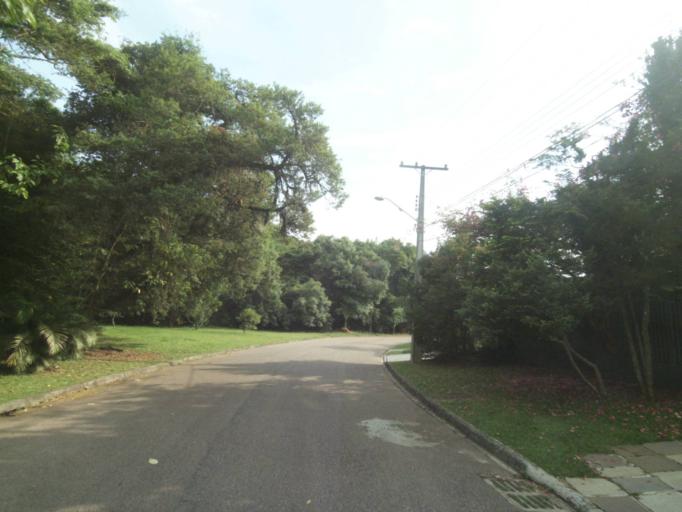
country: BR
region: Parana
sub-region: Curitiba
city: Curitiba
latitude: -25.4158
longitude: -49.3102
